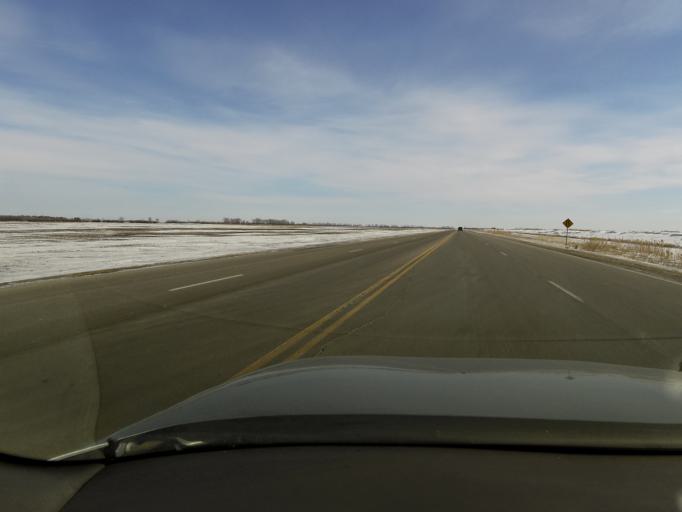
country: US
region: North Dakota
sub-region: Walsh County
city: Grafton
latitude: 48.4127
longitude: -97.3848
